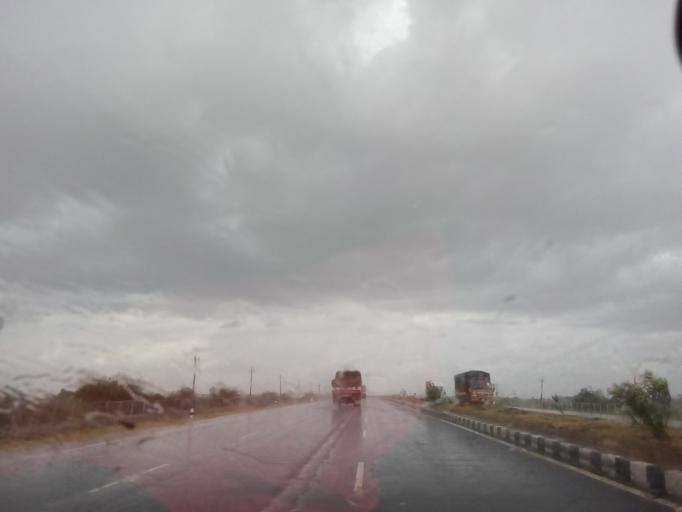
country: IN
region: Karnataka
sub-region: Chitradurga
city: Chitradurga
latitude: 14.1206
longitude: 76.5162
